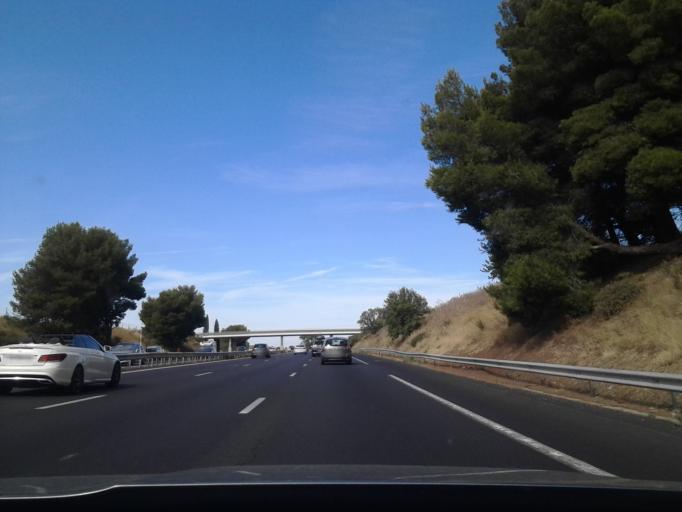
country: FR
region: Languedoc-Roussillon
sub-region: Departement de l'Herault
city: Pomerols
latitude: 43.4074
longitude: 3.4922
